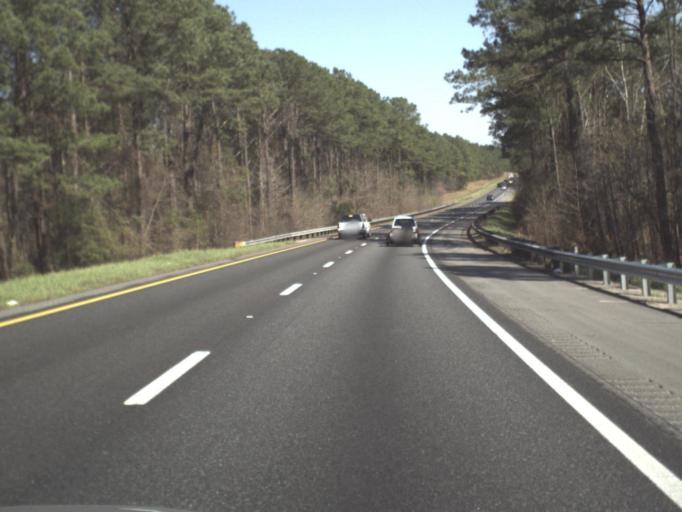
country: US
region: Florida
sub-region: Gadsden County
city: Chattahoochee
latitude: 30.6318
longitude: -84.8726
